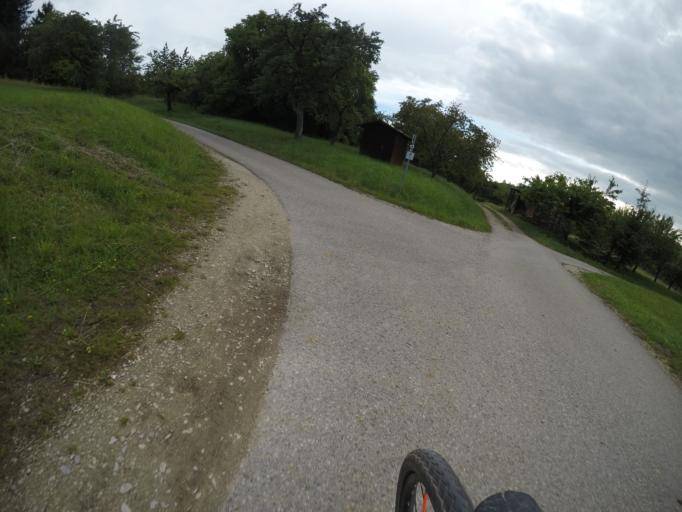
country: DE
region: Baden-Wuerttemberg
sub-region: Regierungsbezirk Stuttgart
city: Kohlberg
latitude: 48.5540
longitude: 9.3262
